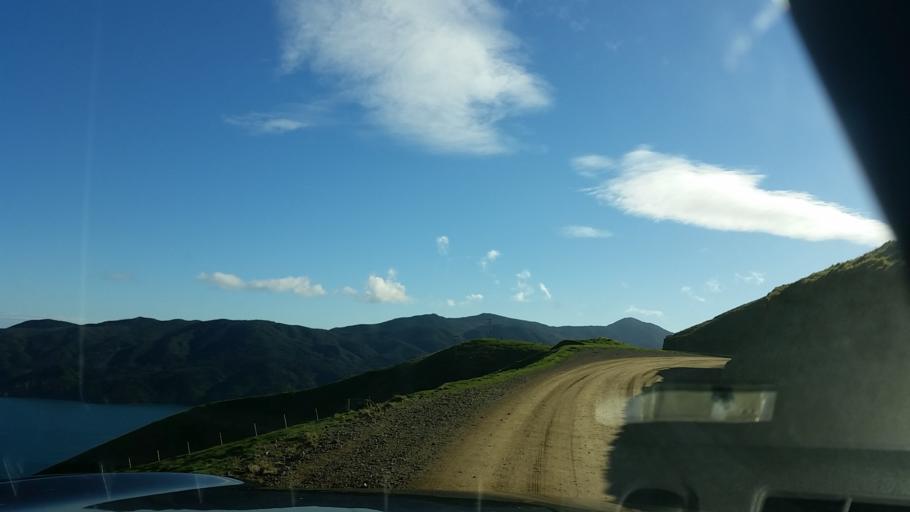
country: NZ
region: Marlborough
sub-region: Marlborough District
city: Picton
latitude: -40.9470
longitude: 173.8376
